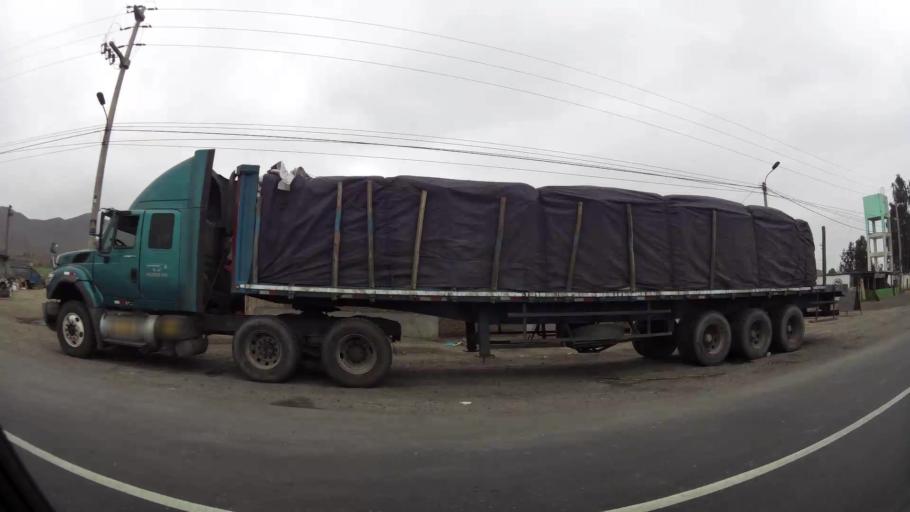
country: PE
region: Lima
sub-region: Barranca
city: Pativilca
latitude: -10.6714
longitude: -77.7936
